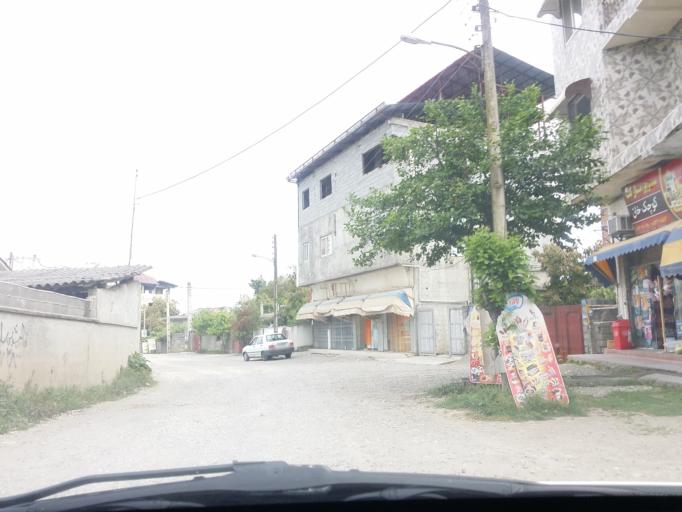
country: IR
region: Mazandaran
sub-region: Nowshahr
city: Nowshahr
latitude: 36.6230
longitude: 51.4938
